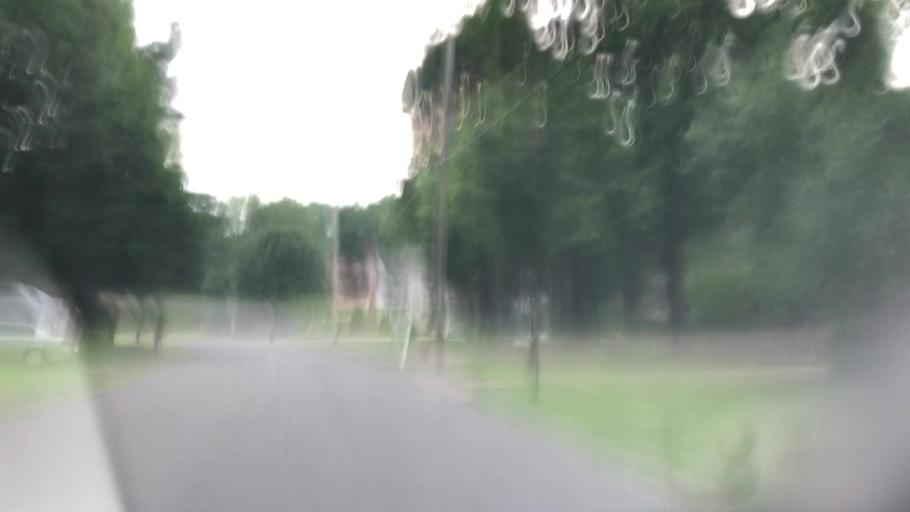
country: US
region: Ohio
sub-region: Stark County
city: North Canton
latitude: 40.8528
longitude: -81.3877
